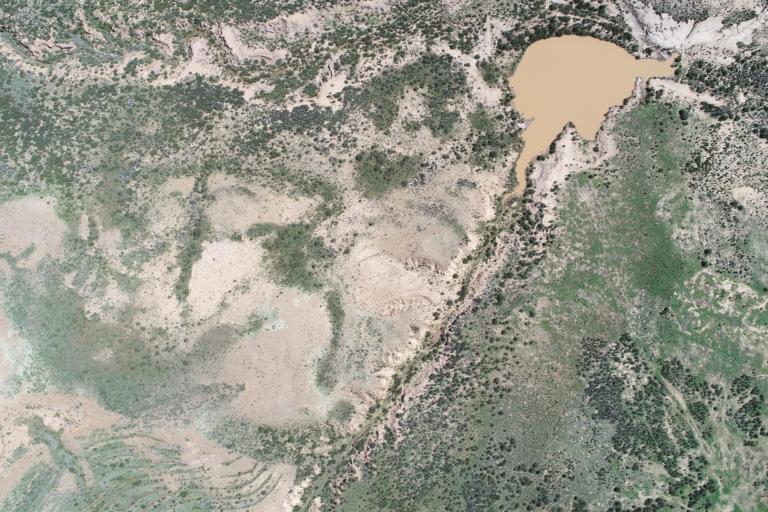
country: BO
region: La Paz
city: Curahuara de Carangas
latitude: -17.2945
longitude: -68.5107
